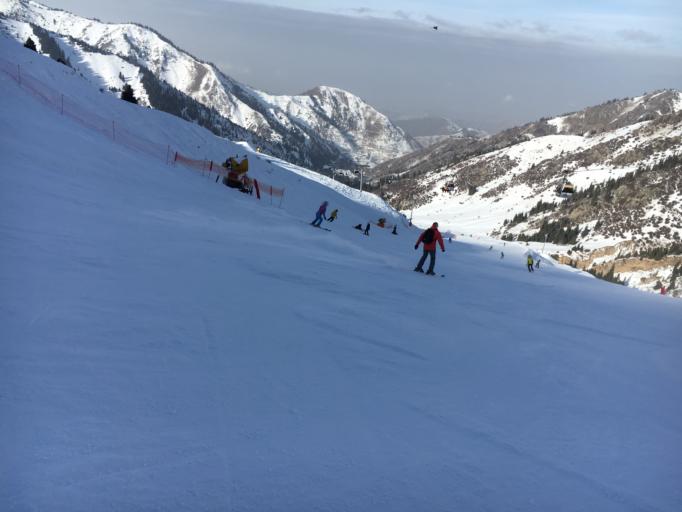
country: KZ
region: Almaty Qalasy
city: Almaty
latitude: 43.1205
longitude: 77.0959
